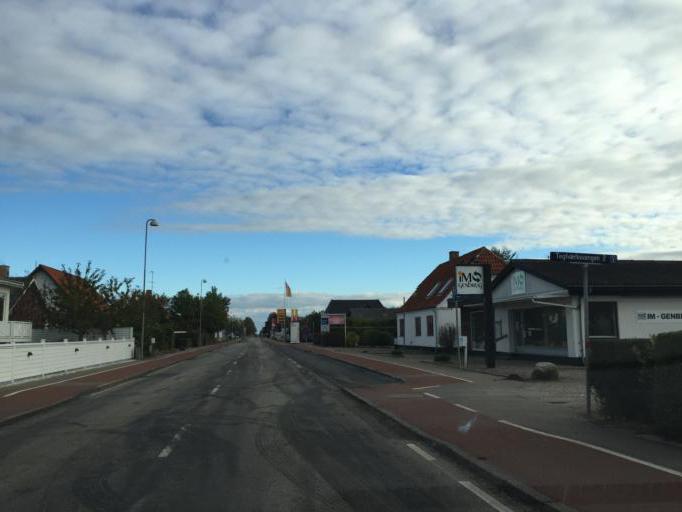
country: DK
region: Zealand
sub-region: Odsherred Kommune
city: Horve
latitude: 55.7873
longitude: 11.4655
